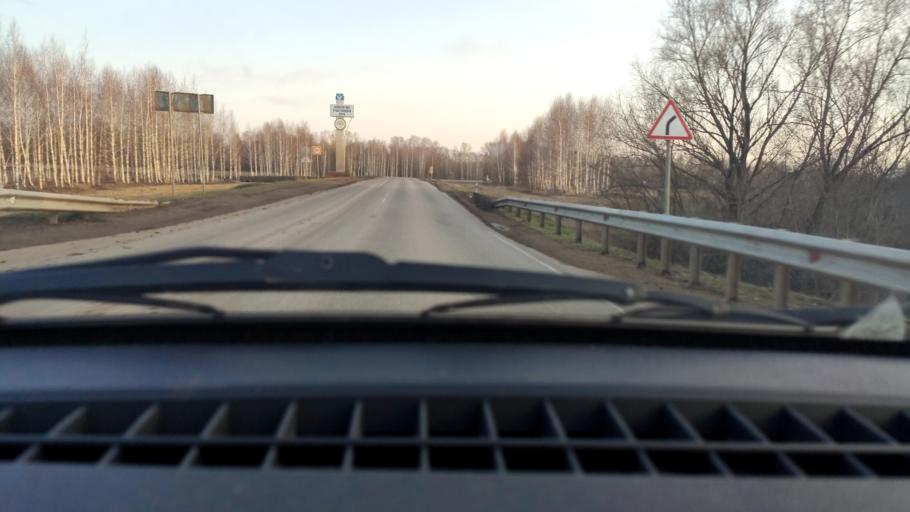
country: RU
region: Bashkortostan
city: Davlekanovo
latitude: 54.3656
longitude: 55.1954
